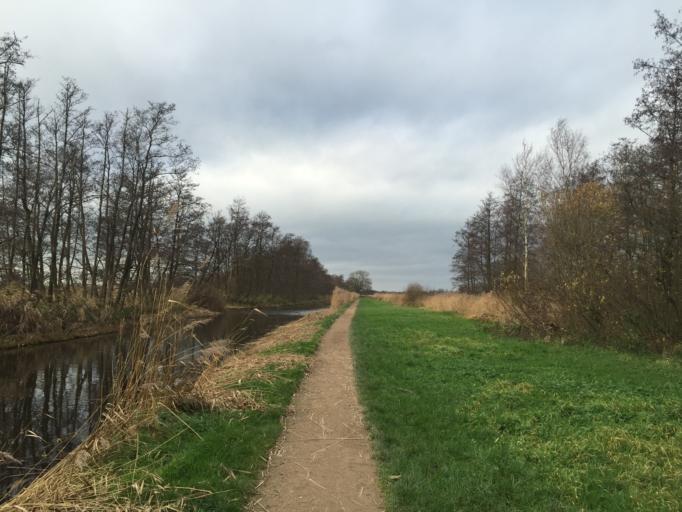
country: NL
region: North Holland
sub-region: Gemeente Wijdemeren
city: Kortenhoef
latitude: 52.2600
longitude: 5.0934
